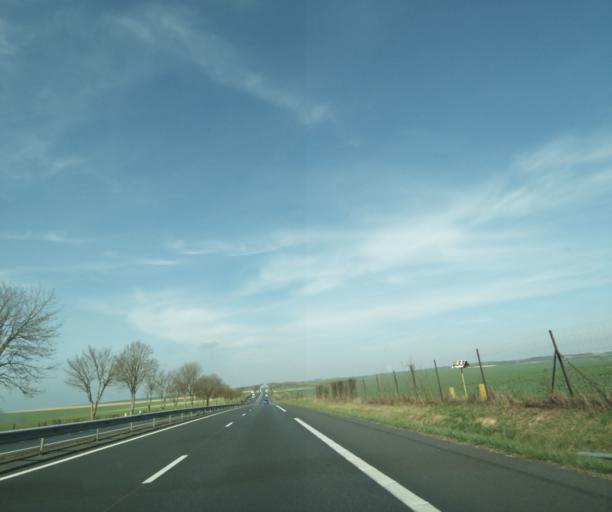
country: FR
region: Centre
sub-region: Departement de l'Indre
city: Montierchaume
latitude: 46.9648
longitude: 1.7615
